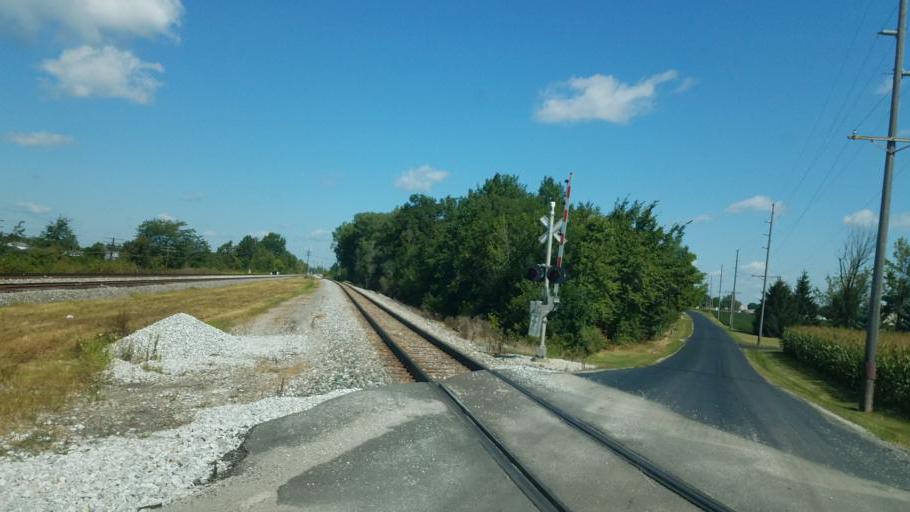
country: US
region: Ohio
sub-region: Wyandot County
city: Carey
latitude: 40.9419
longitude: -83.3674
